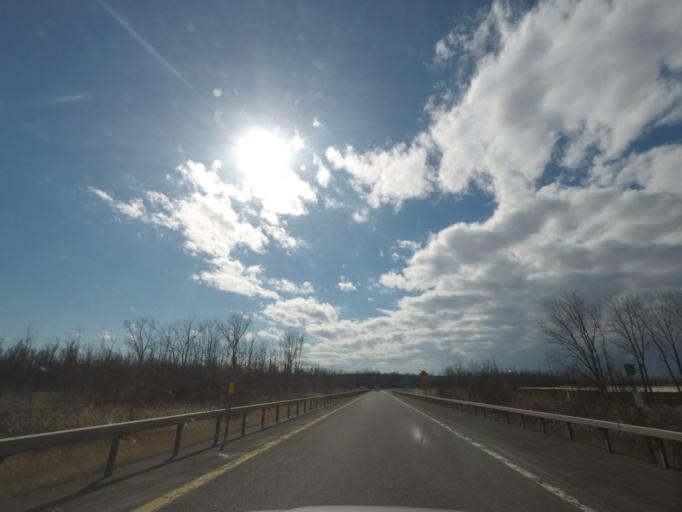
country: US
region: New York
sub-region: Onondaga County
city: East Syracuse
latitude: 43.0581
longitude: -76.0558
